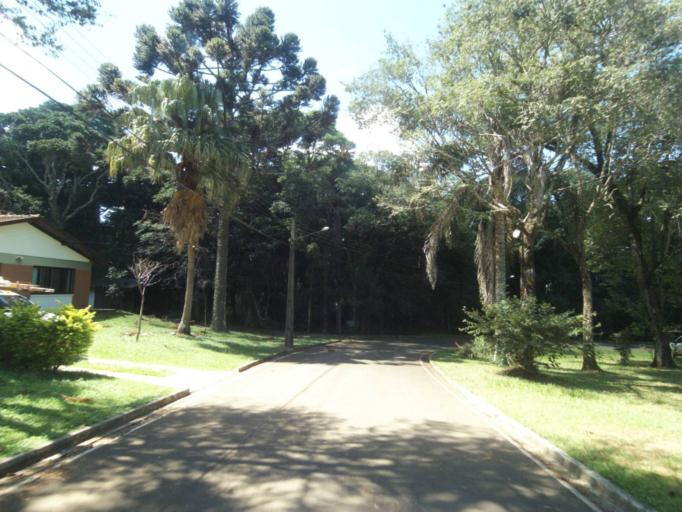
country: BR
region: Parana
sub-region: Chopinzinho
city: Chopinzinho
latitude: -25.7978
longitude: -52.0935
